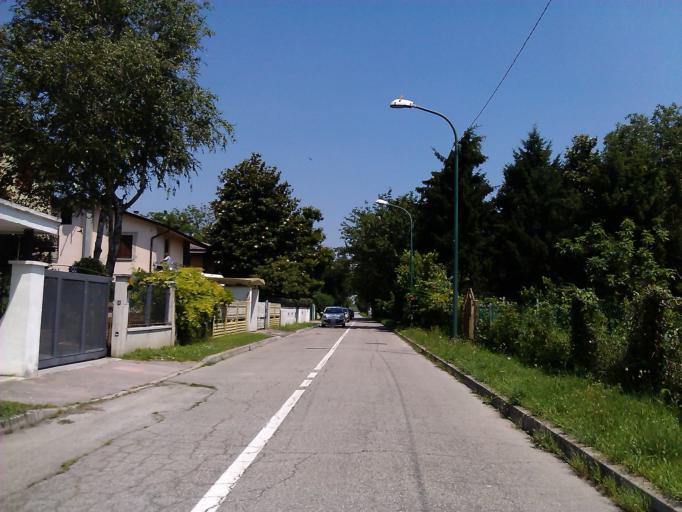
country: IT
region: Veneto
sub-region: Provincia di Venezia
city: Fornase
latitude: 45.4550
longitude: 12.1862
